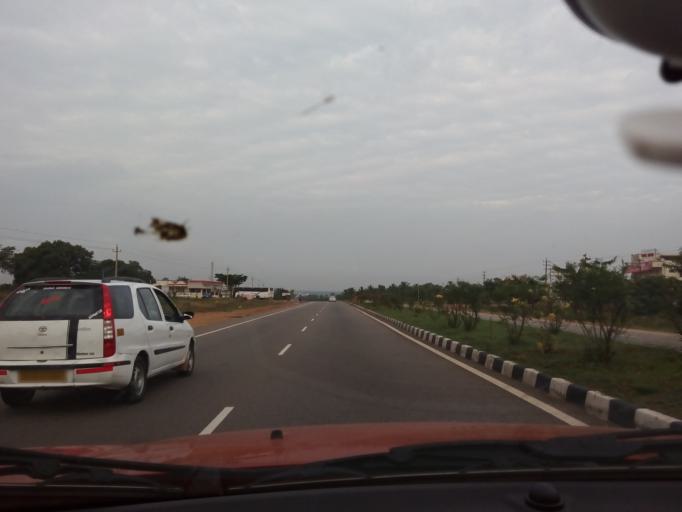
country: IN
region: Karnataka
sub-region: Mandya
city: Belluru
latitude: 12.9879
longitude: 76.8757
